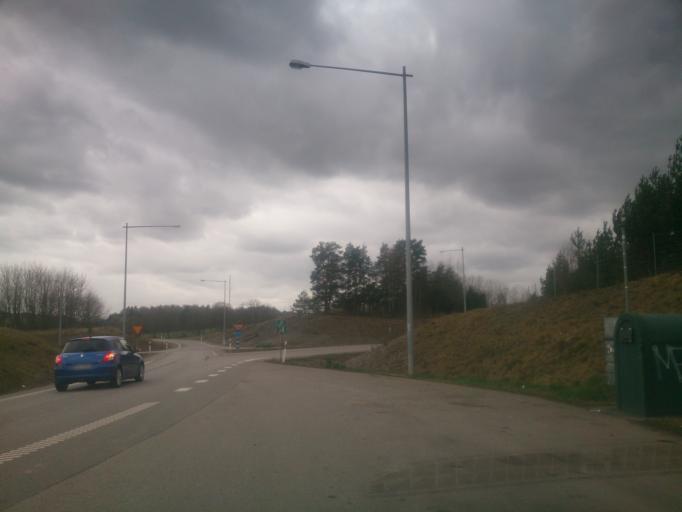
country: SE
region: OEstergoetland
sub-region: Norrkopings Kommun
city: Norrkoping
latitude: 58.5702
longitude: 16.0770
